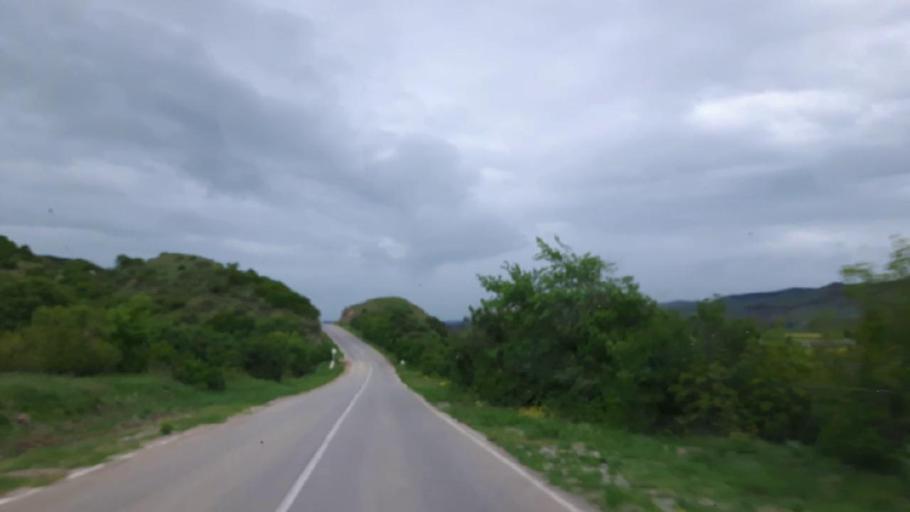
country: GE
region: Shida Kartli
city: Gori
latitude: 41.9891
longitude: 44.0416
